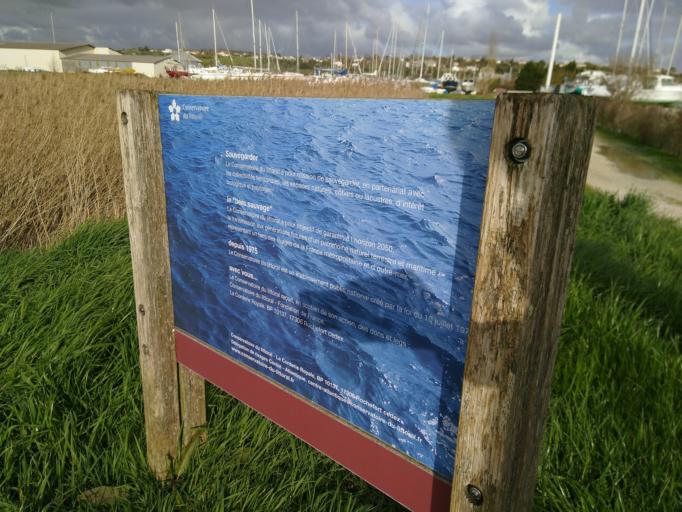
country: FR
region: Poitou-Charentes
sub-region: Departement de la Charente-Maritime
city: Mortagne-sur-Gironde
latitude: 45.4750
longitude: -0.8009
